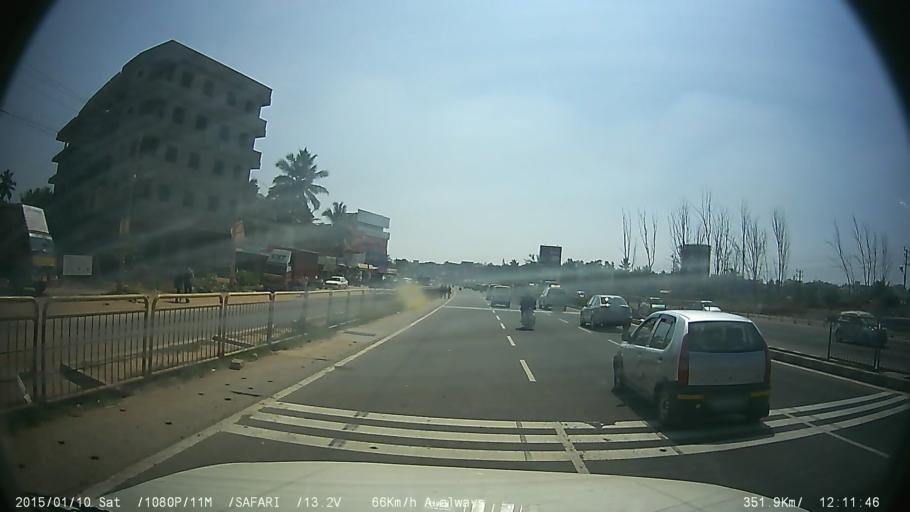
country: IN
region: Karnataka
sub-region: Bangalore Urban
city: Anekal
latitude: 12.8299
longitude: 77.6814
